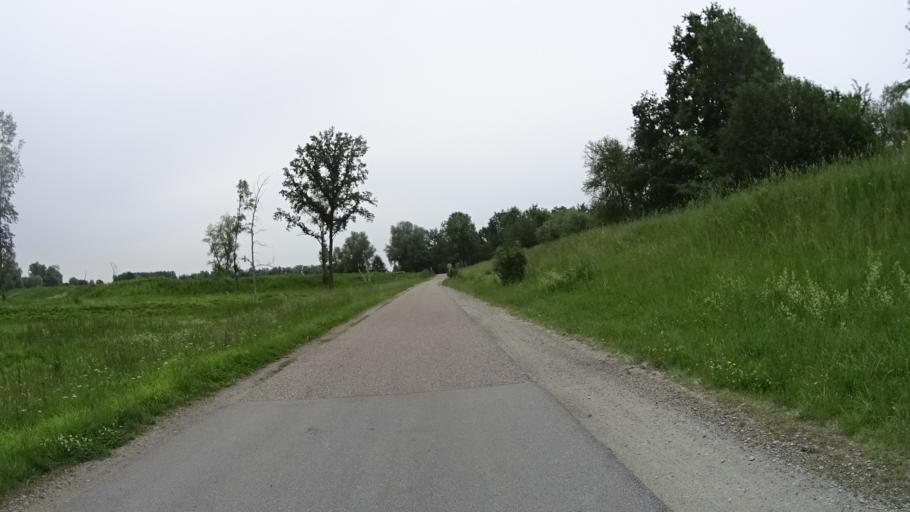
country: DE
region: Bavaria
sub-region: Lower Bavaria
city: Niederalteich
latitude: 48.7873
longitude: 13.0067
